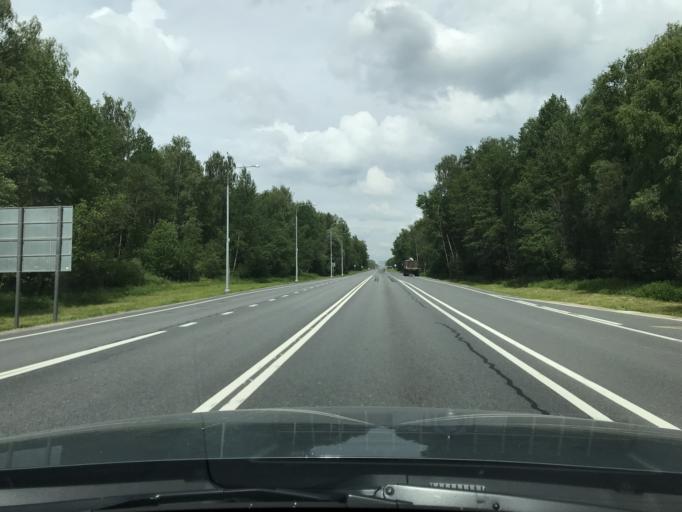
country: RU
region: Kaluga
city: Borovsk
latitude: 55.3681
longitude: 36.4140
